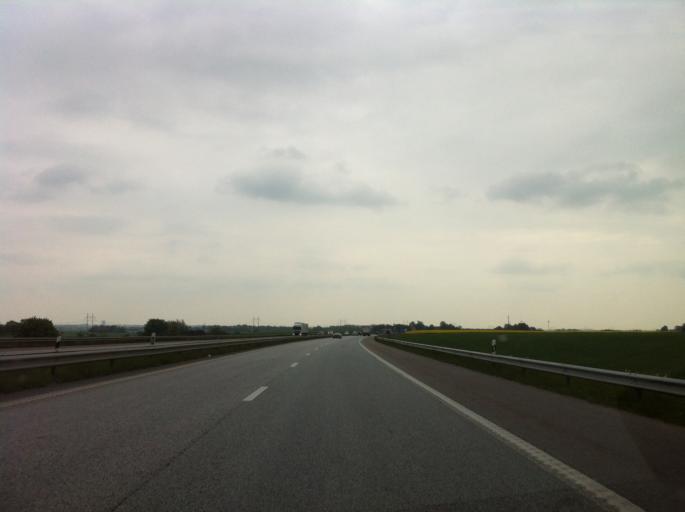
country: SE
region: Skane
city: Bjarred
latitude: 55.7340
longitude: 13.0724
